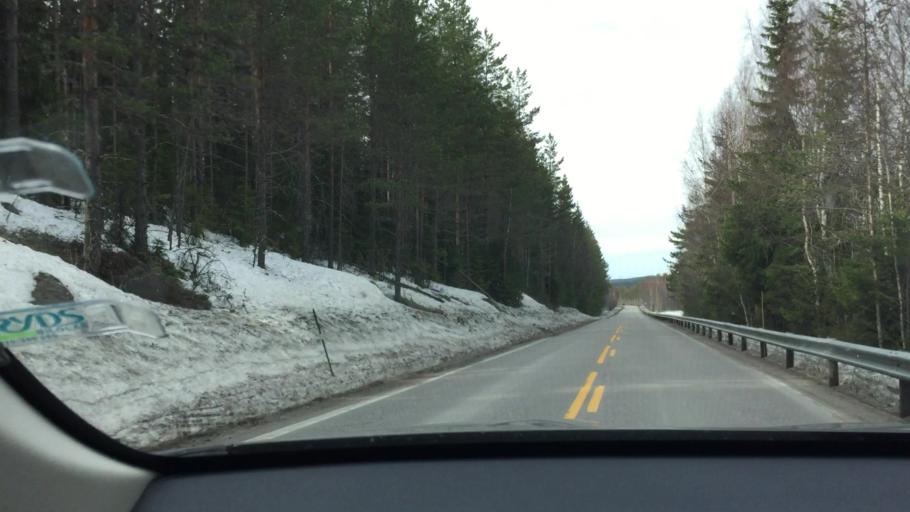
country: NO
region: Hedmark
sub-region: Trysil
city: Innbygda
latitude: 61.0674
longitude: 12.5797
